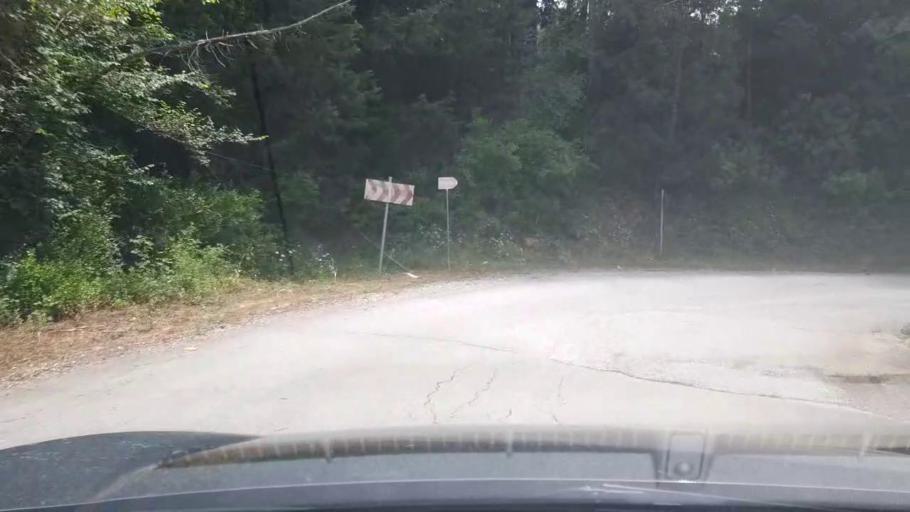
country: GR
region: Ionian Islands
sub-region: Lefkada
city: Nidri
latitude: 38.6452
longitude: 20.7021
